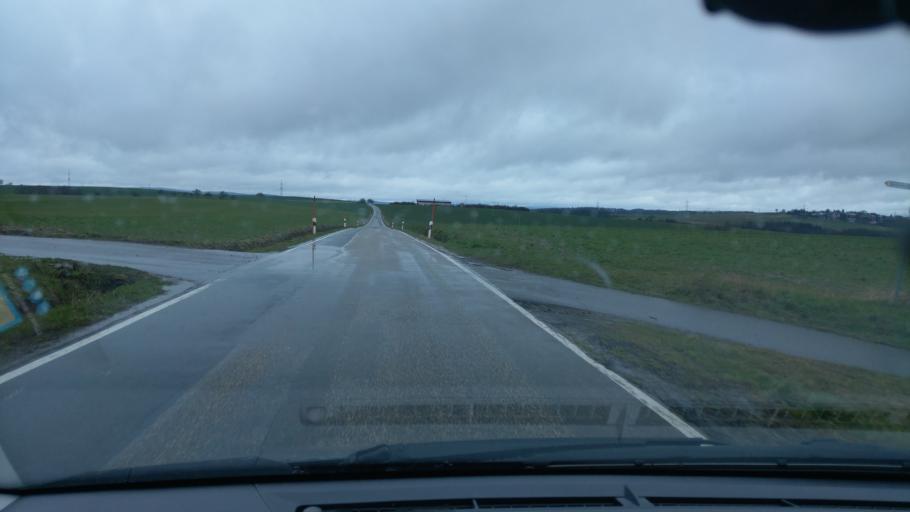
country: DE
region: Rheinland-Pfalz
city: Kleinbundenbach
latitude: 49.3245
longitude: 7.4342
